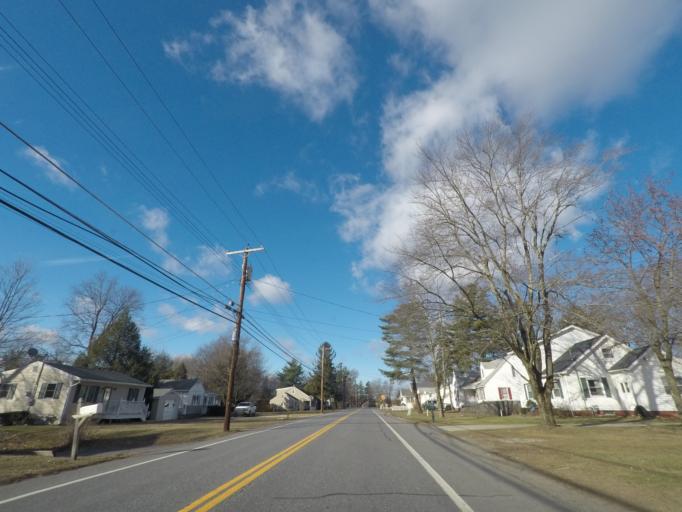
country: US
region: New York
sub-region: Saratoga County
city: Waterford
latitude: 42.8357
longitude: -73.7330
